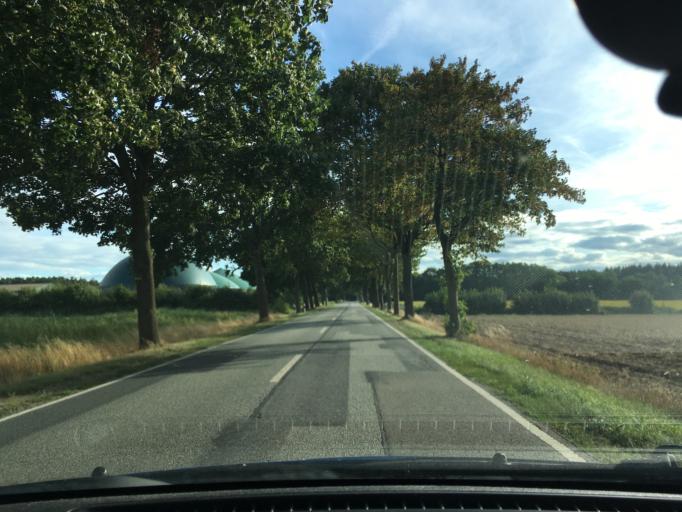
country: DE
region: Lower Saxony
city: Brackel
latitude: 53.3234
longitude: 10.0678
